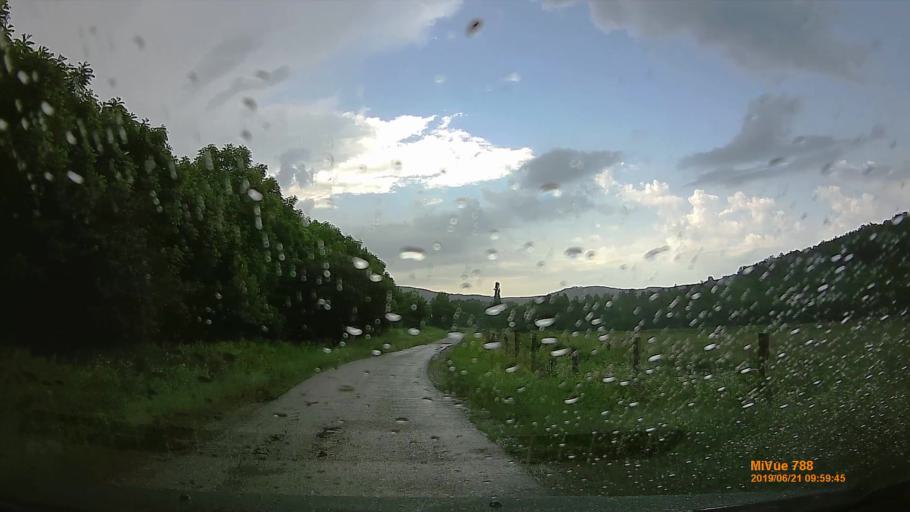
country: HU
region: Baranya
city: Buekkoesd
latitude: 46.2107
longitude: 17.9722
